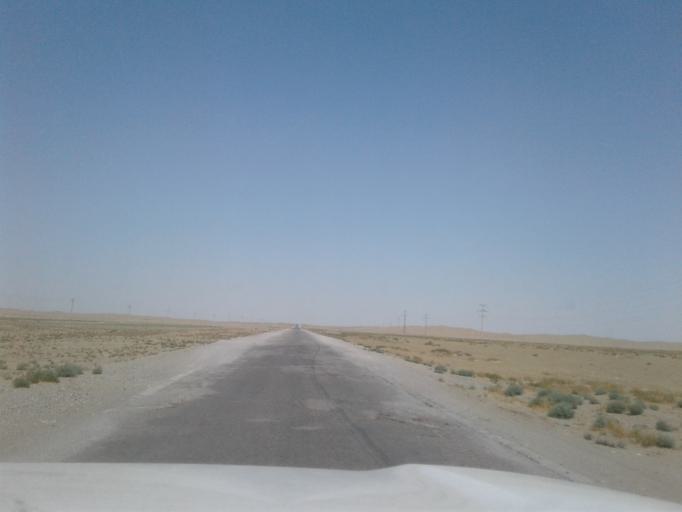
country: TM
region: Balkan
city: Gumdag
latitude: 38.3658
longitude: 54.3842
